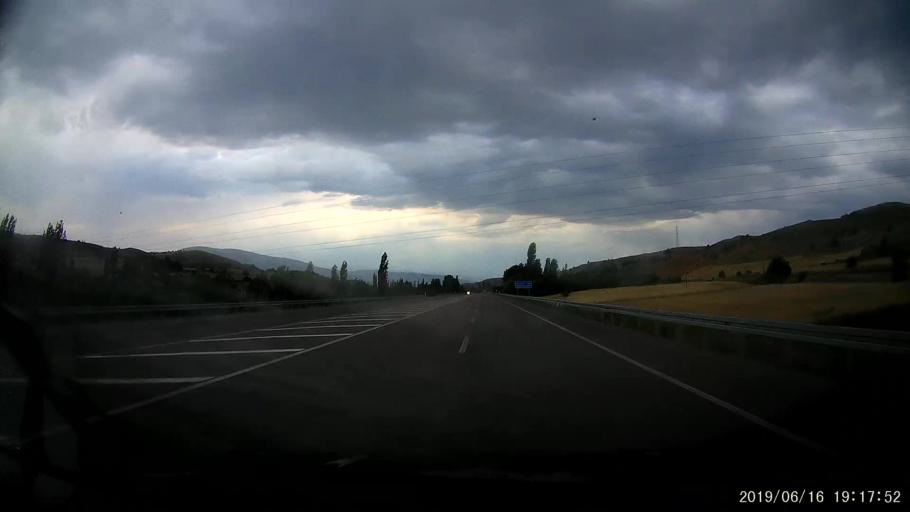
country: TR
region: Sivas
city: Akincilar
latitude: 40.0939
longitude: 38.4742
